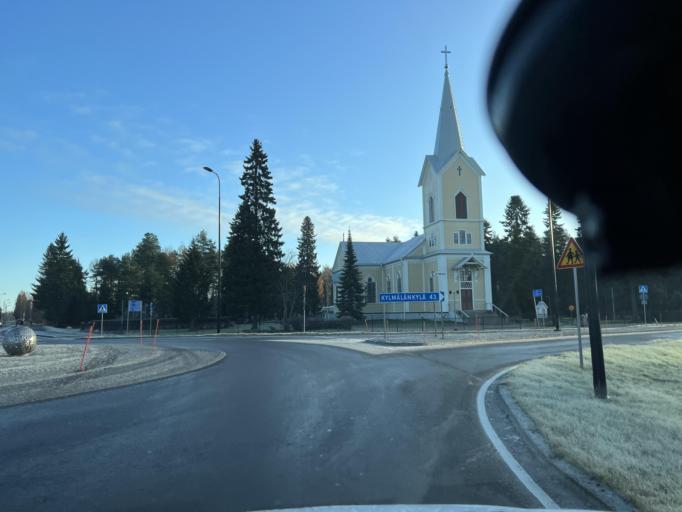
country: FI
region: Northern Ostrobothnia
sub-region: Oulu
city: Tyrnaevae
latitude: 64.7637
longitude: 25.6526
